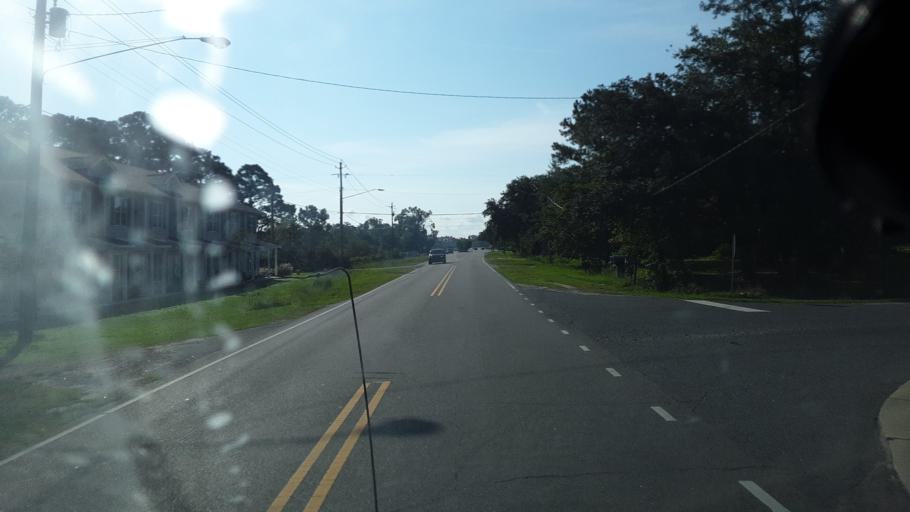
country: US
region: North Carolina
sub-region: Brunswick County
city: Navassa
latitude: 34.2391
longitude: -78.0084
